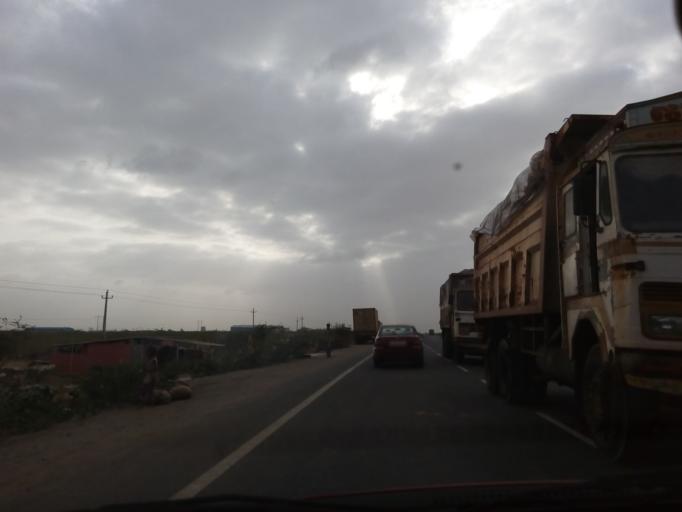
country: IN
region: Gujarat
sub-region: Kachchh
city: Bhuj
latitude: 23.2500
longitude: 69.8572
